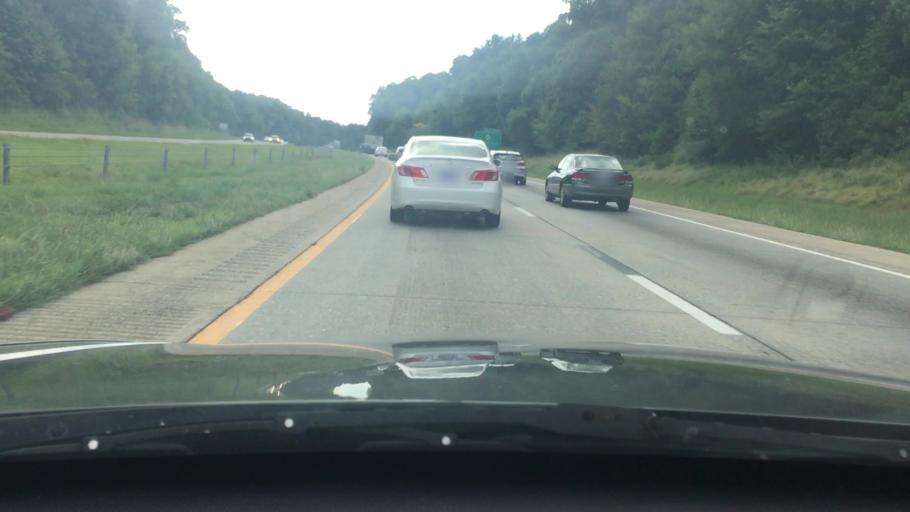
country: US
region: North Carolina
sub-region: Orange County
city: Chapel Hill
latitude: 35.9694
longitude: -79.0414
